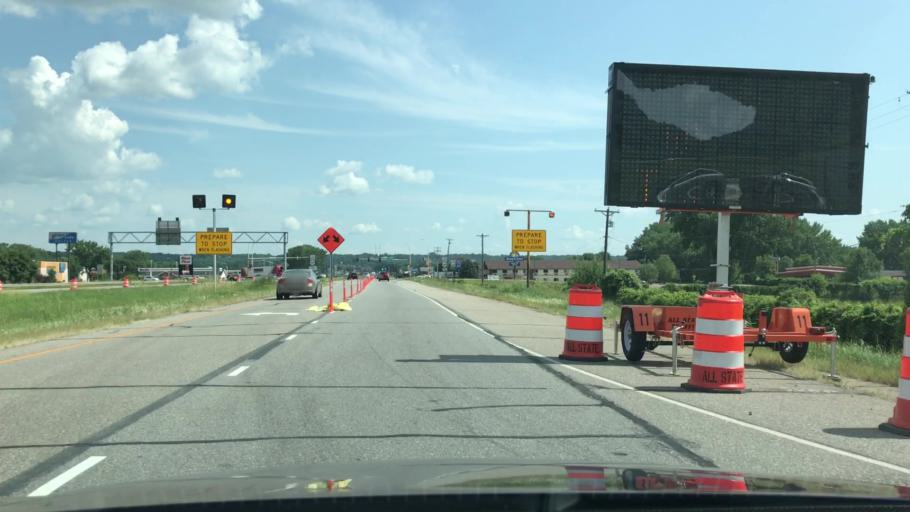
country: US
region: Minnesota
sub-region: Nicollet County
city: North Mankato
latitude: 44.1904
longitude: -94.0161
